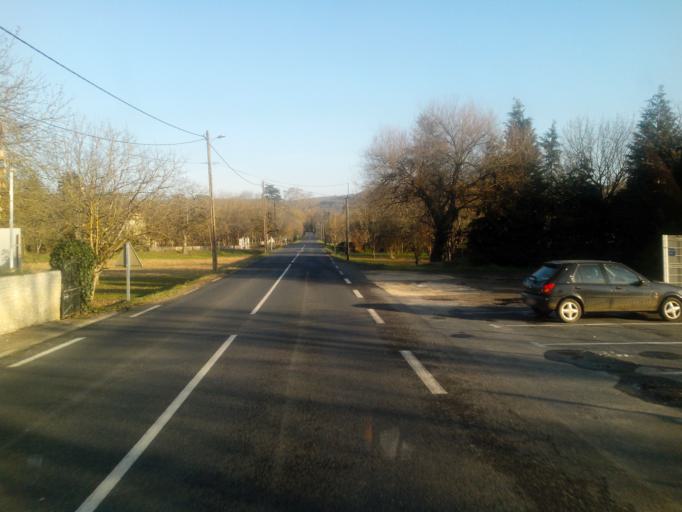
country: FR
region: Midi-Pyrenees
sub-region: Departement du Lot
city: Vayrac
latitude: 44.9082
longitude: 1.6306
